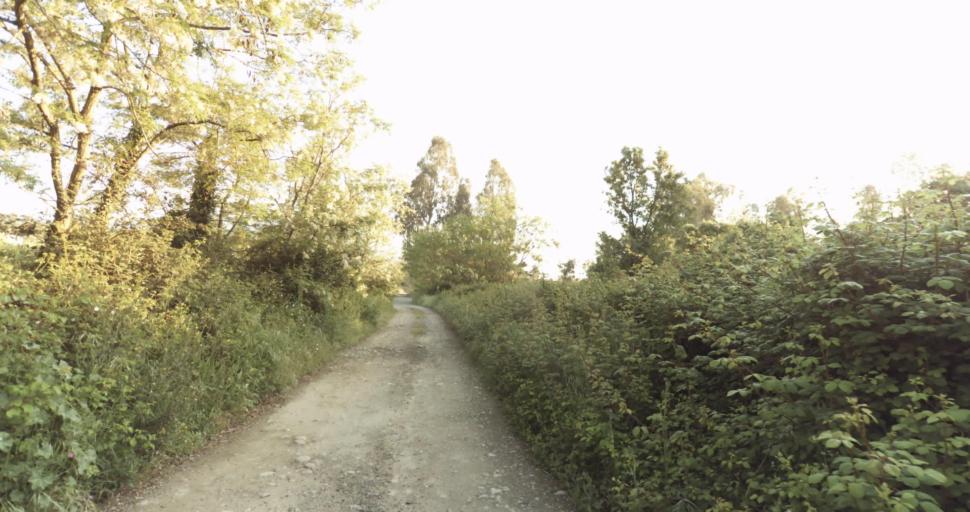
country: FR
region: Corsica
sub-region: Departement de la Haute-Corse
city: Biguglia
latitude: 42.6326
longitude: 9.4406
